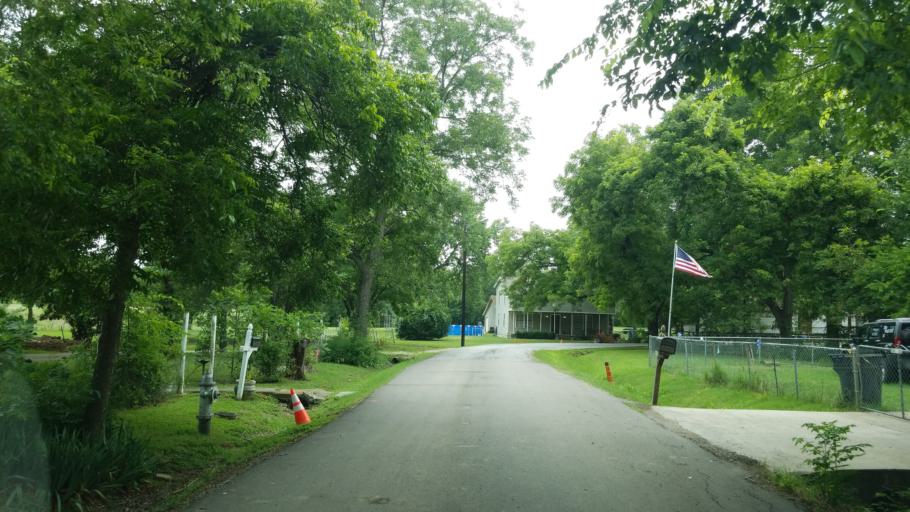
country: US
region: Texas
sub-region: Dallas County
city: Cockrell Hill
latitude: 32.7918
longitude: -96.8926
